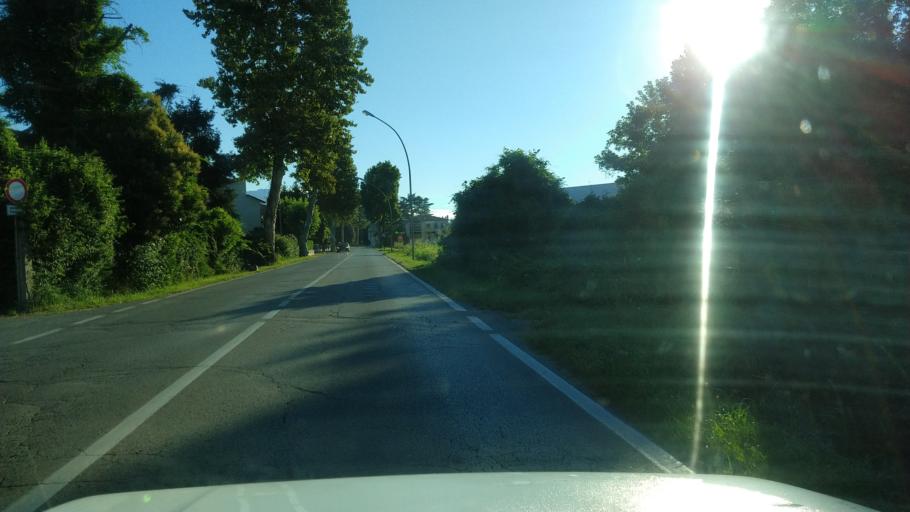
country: IT
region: Veneto
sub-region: Provincia di Vicenza
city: Marostica
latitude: 45.7382
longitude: 11.6558
